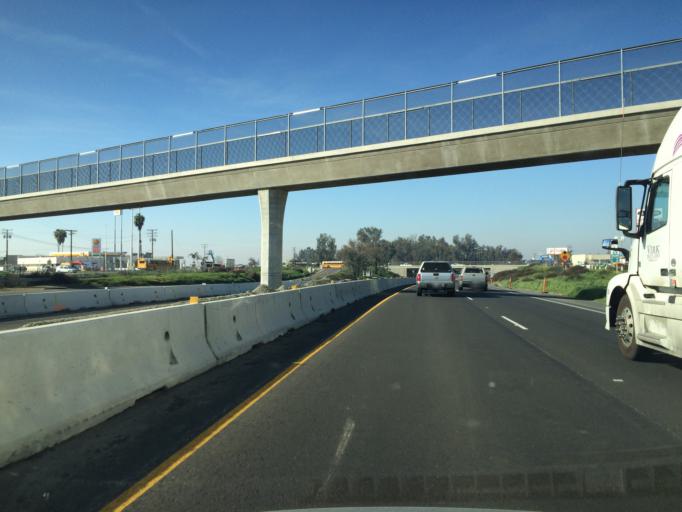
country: US
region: California
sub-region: Tulare County
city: Goshen
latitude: 36.3484
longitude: -119.4254
